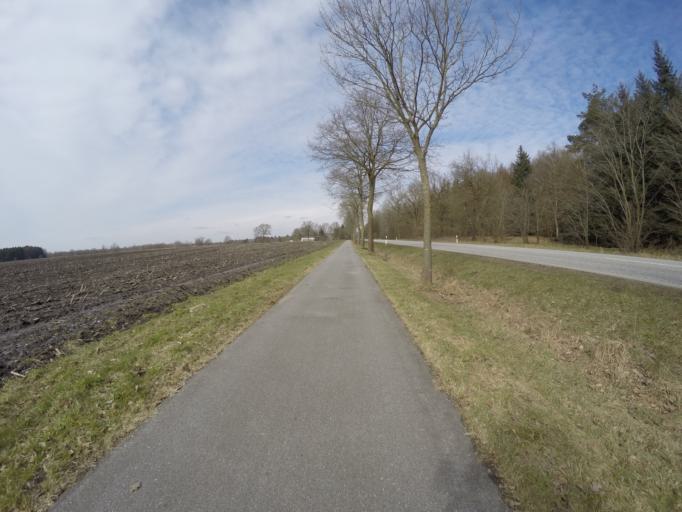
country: DE
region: Schleswig-Holstein
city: Heidmoor
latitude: 53.8246
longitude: 9.8825
